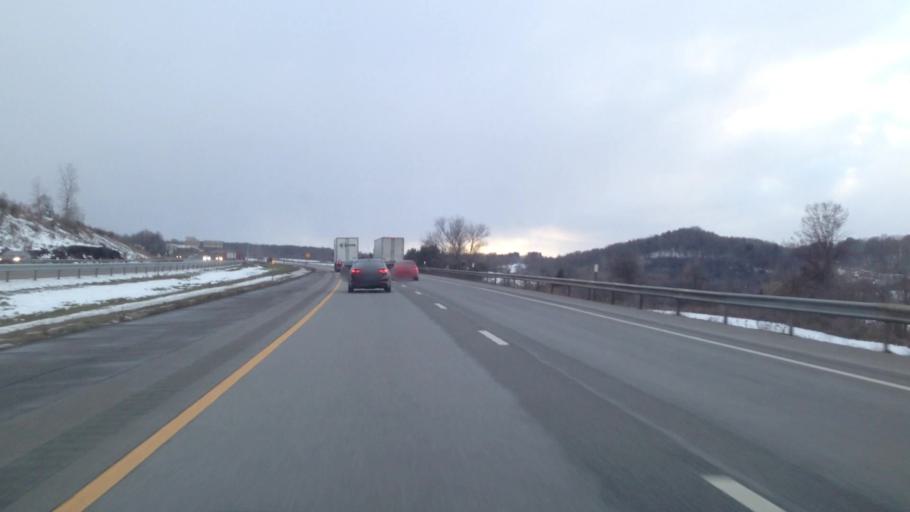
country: US
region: New York
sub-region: Herkimer County
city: Little Falls
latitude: 43.0166
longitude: -74.8194
